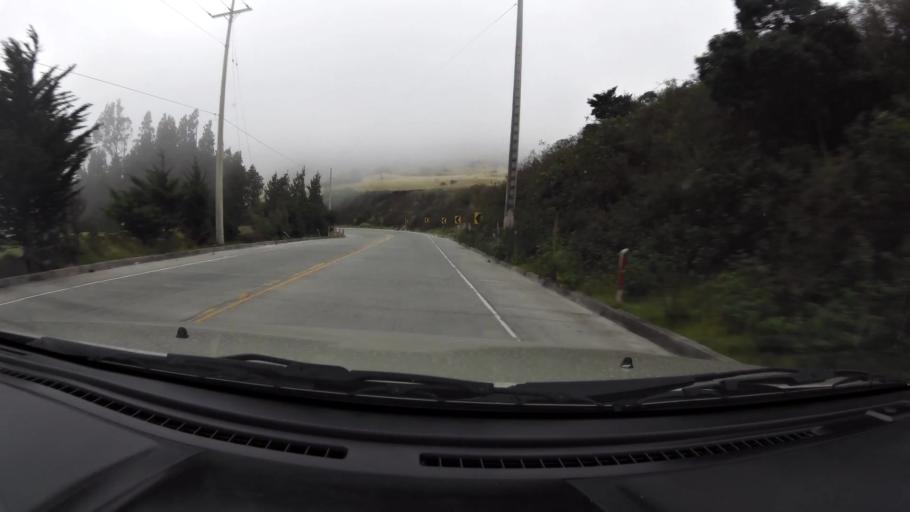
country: EC
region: Canar
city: Canar
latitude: -2.4848
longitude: -79.0014
